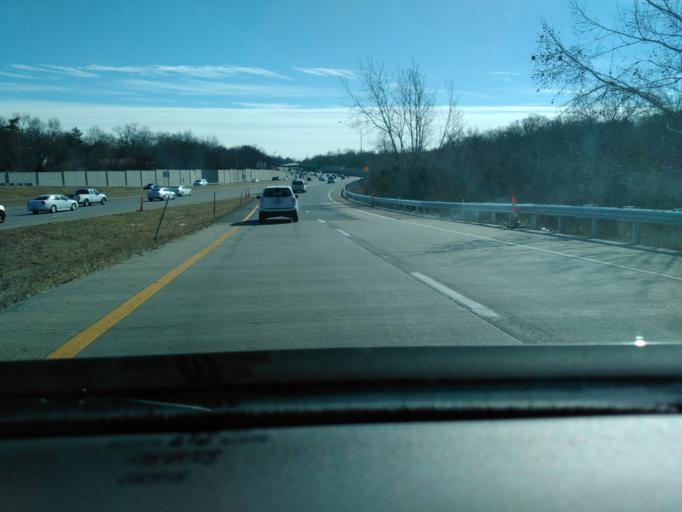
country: US
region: Missouri
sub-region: Saint Louis County
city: Des Peres
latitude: 38.5807
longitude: -90.4482
